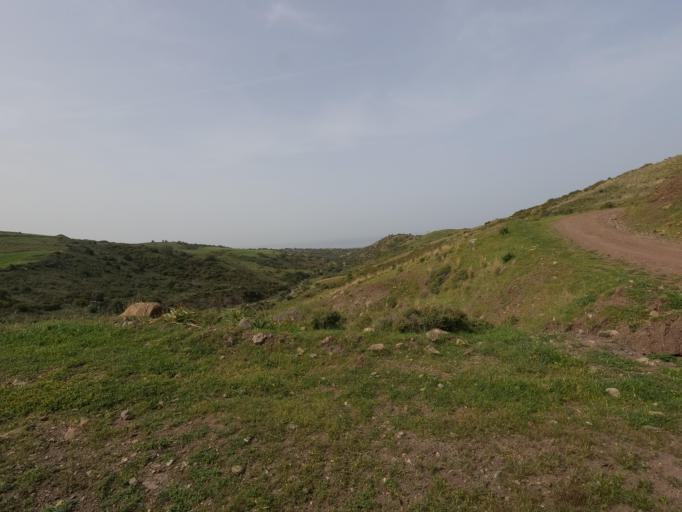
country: CY
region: Pafos
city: Pegeia
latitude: 34.9553
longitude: 32.3409
